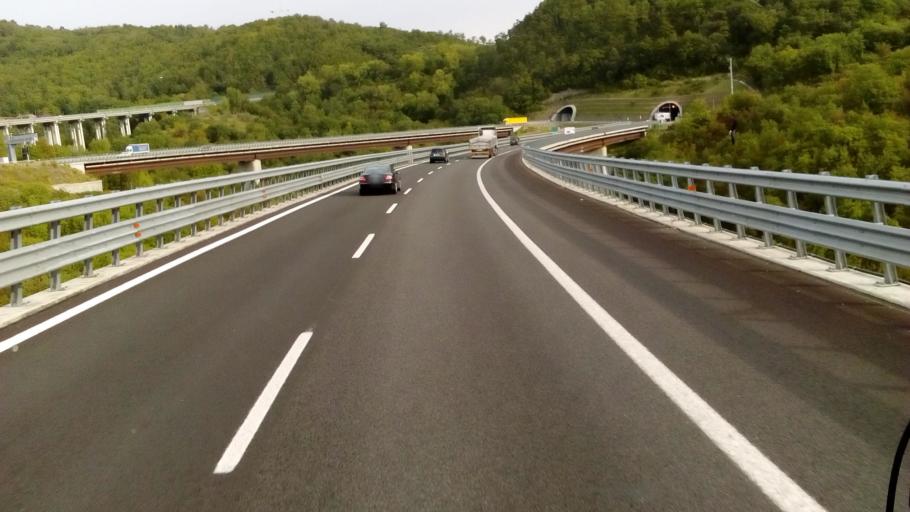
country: IT
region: Tuscany
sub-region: Province of Florence
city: Barberino di Mugello
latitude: 44.0348
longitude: 11.2264
